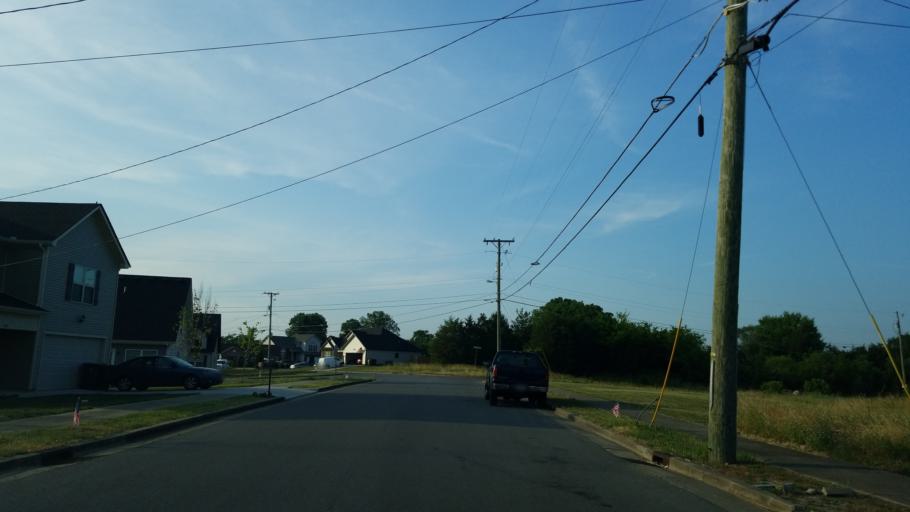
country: US
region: Tennessee
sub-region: Rutherford County
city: La Vergne
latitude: 36.0499
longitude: -86.5898
